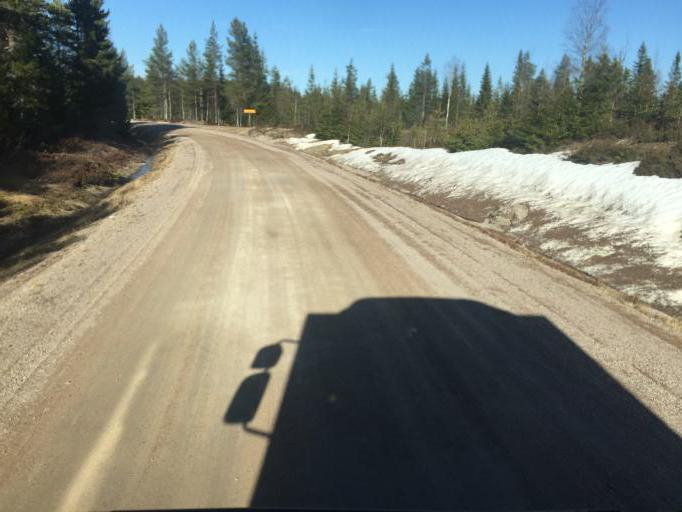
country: SE
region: Vaermland
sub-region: Filipstads Kommun
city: Lesjofors
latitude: 60.2468
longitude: 14.0385
